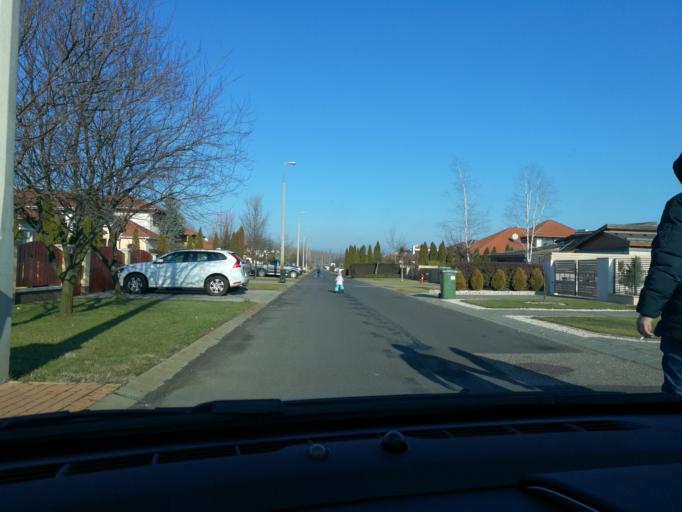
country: HU
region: Szabolcs-Szatmar-Bereg
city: Nyiregyhaza
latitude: 47.9746
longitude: 21.7328
